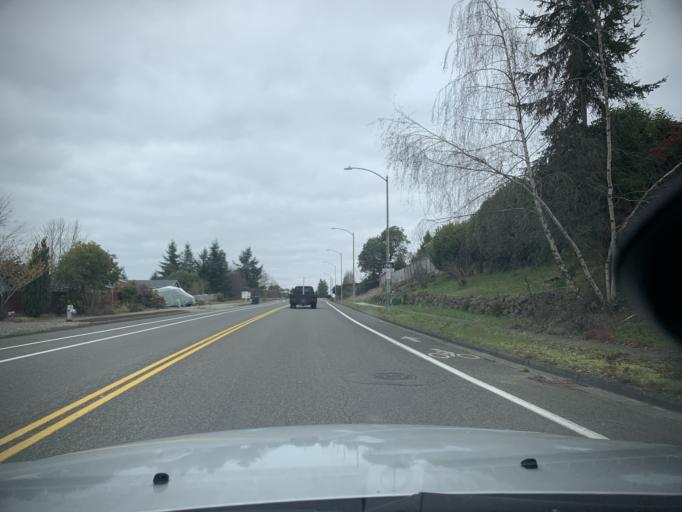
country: US
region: Washington
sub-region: Pierce County
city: Fircrest
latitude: 47.2754
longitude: -122.5238
